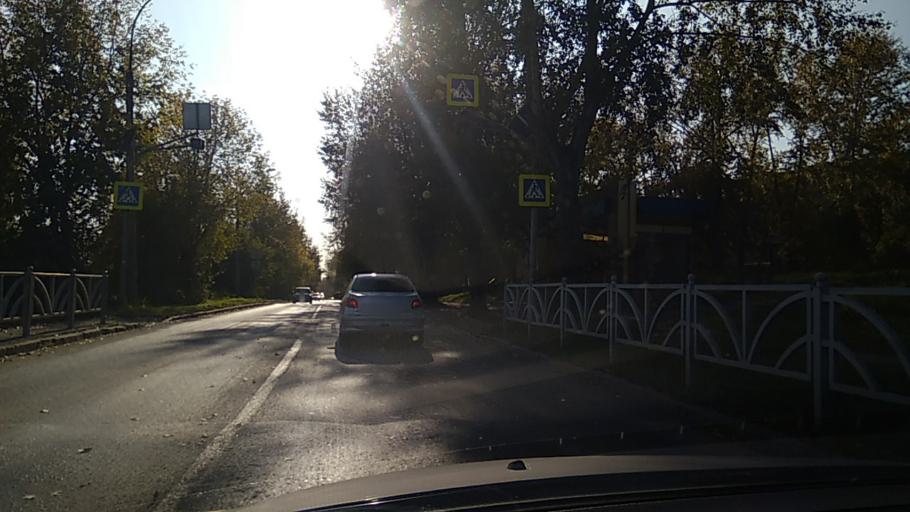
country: RU
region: Sverdlovsk
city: Yekaterinburg
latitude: 56.7768
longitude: 60.6396
